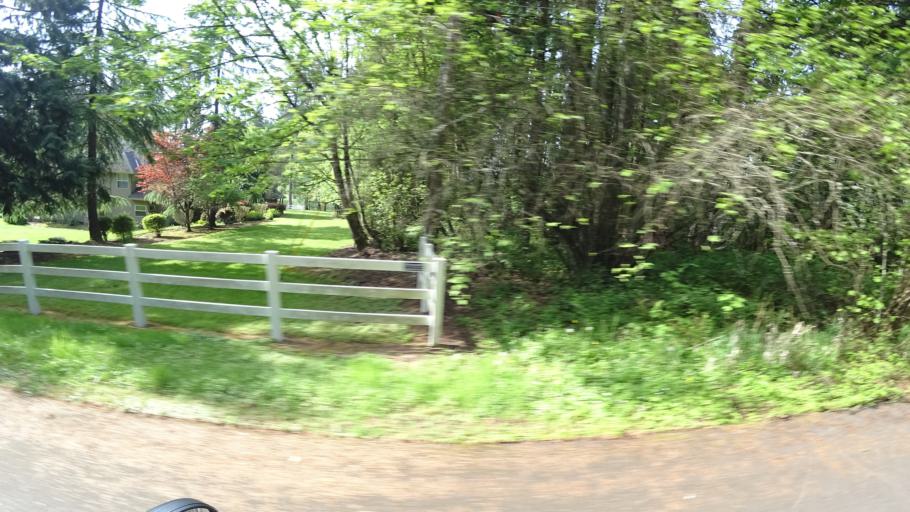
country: US
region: Oregon
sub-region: Washington County
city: King City
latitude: 45.4378
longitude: -122.8480
